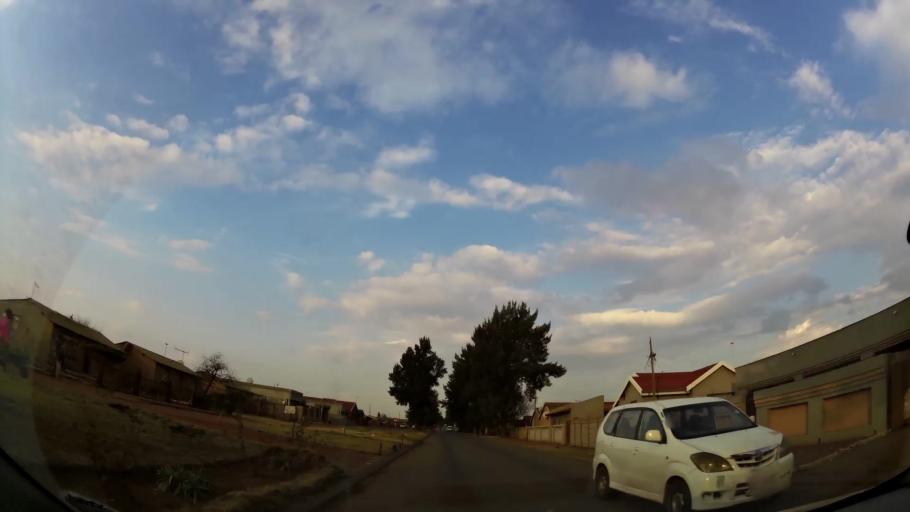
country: ZA
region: Gauteng
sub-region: City of Johannesburg Metropolitan Municipality
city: Orange Farm
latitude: -26.5937
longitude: 27.8296
